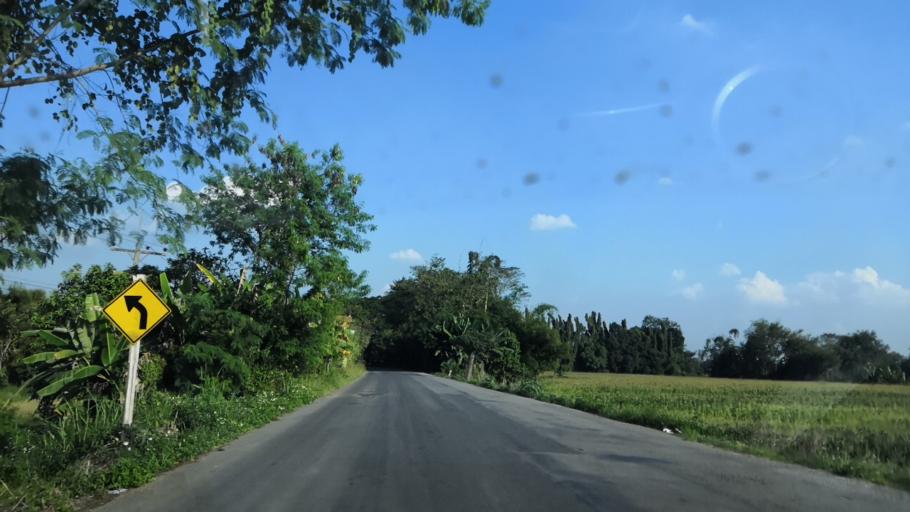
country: TH
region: Chiang Rai
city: Wiang Chai
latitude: 19.9474
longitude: 99.9248
